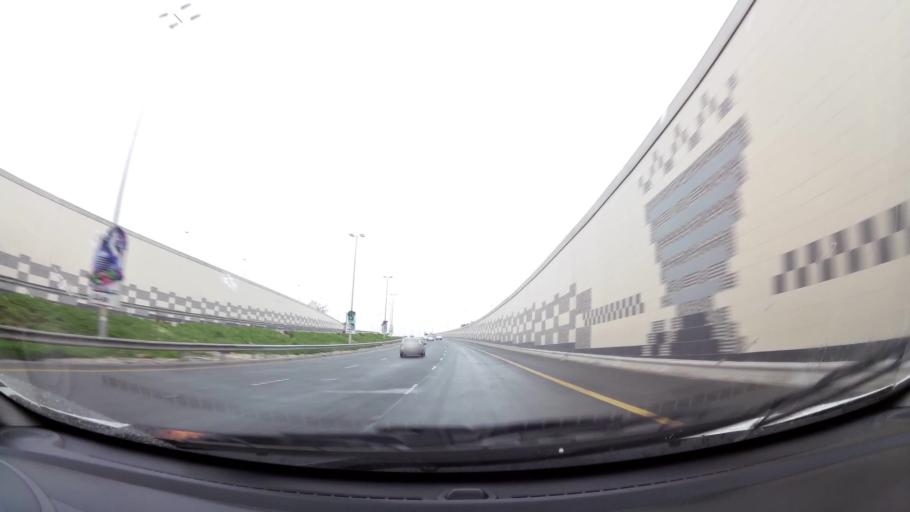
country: BH
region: Central Governorate
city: Madinat Hamad
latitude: 26.0971
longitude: 50.5116
